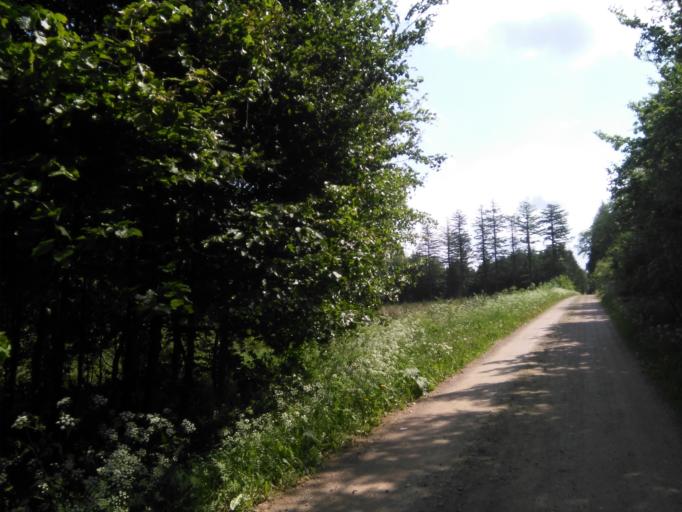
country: DK
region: Central Jutland
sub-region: Favrskov Kommune
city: Hinnerup
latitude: 56.2647
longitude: 10.0398
